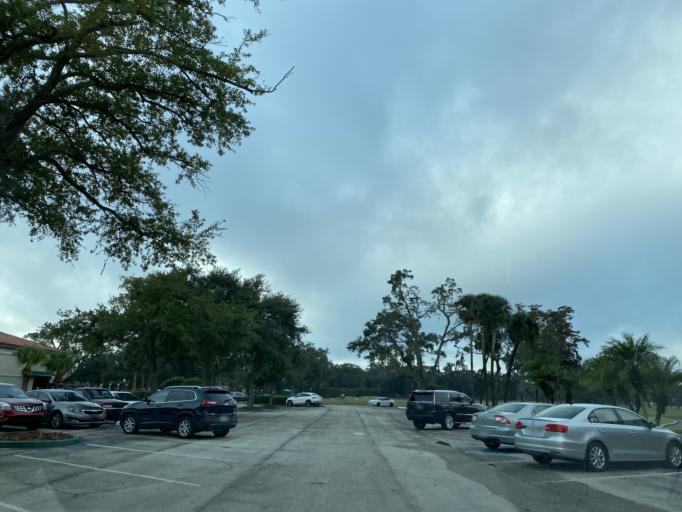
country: US
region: Florida
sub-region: Orange County
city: Fairview Shores
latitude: 28.5613
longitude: -81.4026
